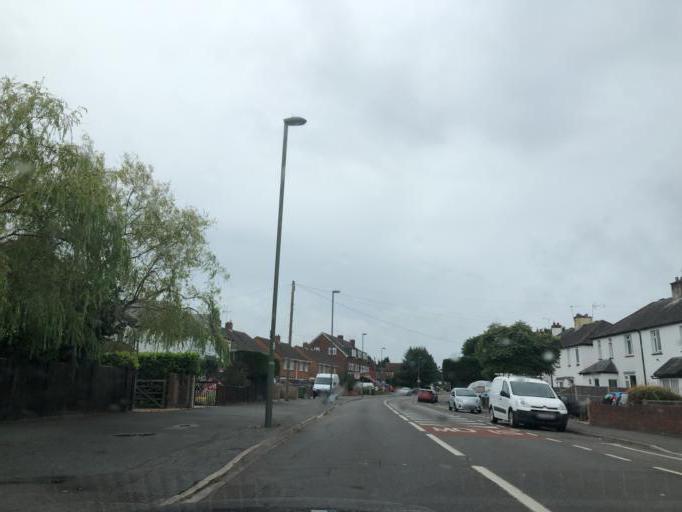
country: GB
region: England
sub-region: Surrey
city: Frimley
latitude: 51.2948
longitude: -0.7266
